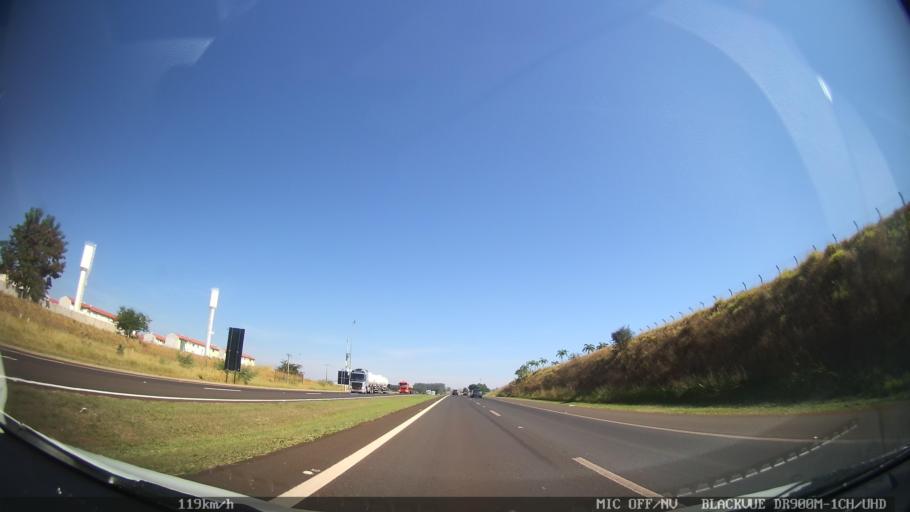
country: BR
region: Sao Paulo
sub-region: Ribeirao Preto
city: Ribeirao Preto
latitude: -21.1126
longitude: -47.8203
